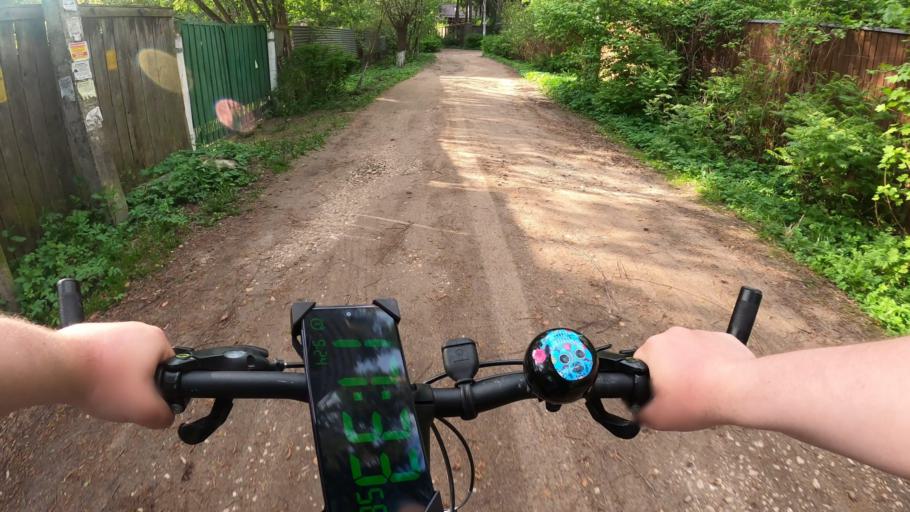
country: RU
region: Moskovskaya
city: Kratovo
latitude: 55.5767
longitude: 38.1756
